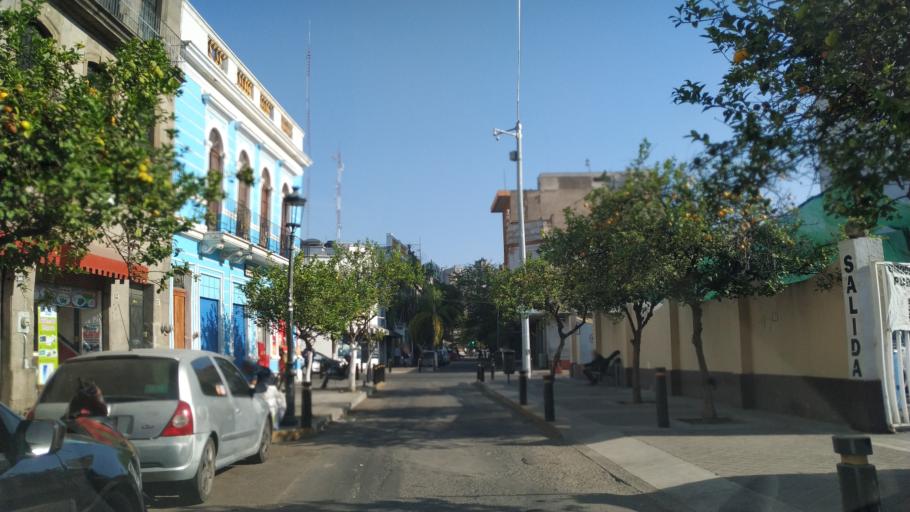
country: MX
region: Jalisco
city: Guadalajara
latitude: 20.6708
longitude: -103.3483
